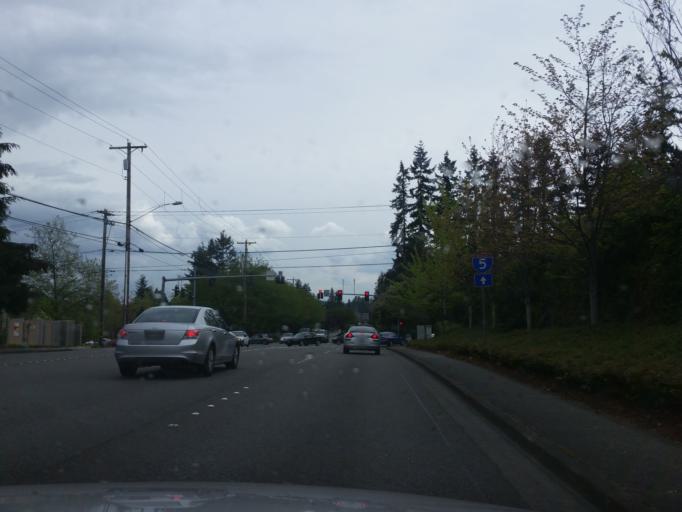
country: US
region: Washington
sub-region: Snohomish County
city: Alderwood Manor
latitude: 47.8290
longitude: -122.2818
